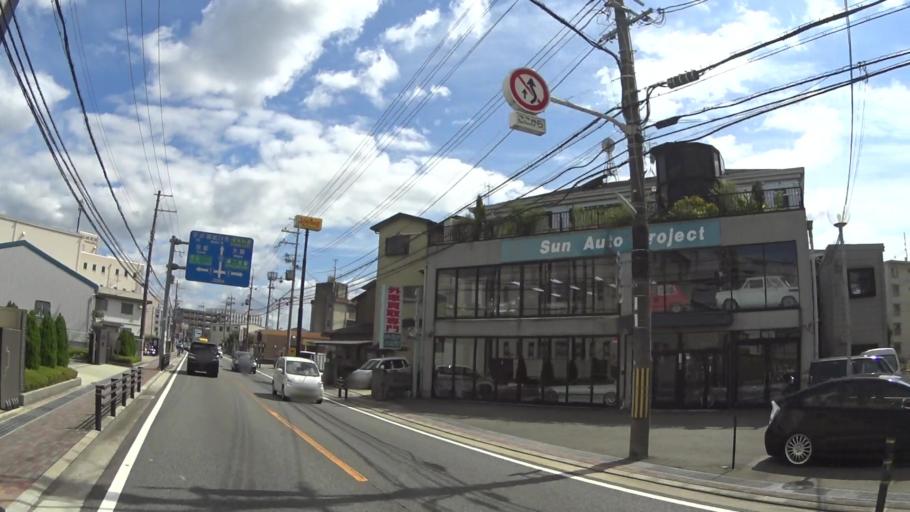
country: JP
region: Kyoto
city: Yawata
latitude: 34.8765
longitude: 135.7432
